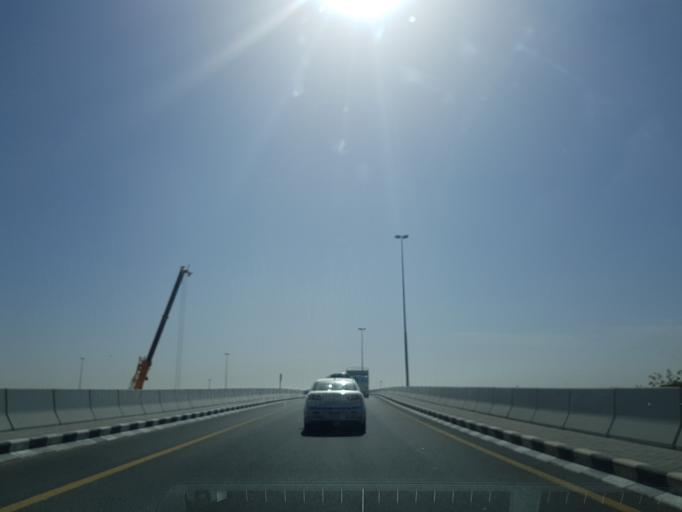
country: AE
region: Dubai
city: Dubai
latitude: 25.0138
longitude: 55.0908
